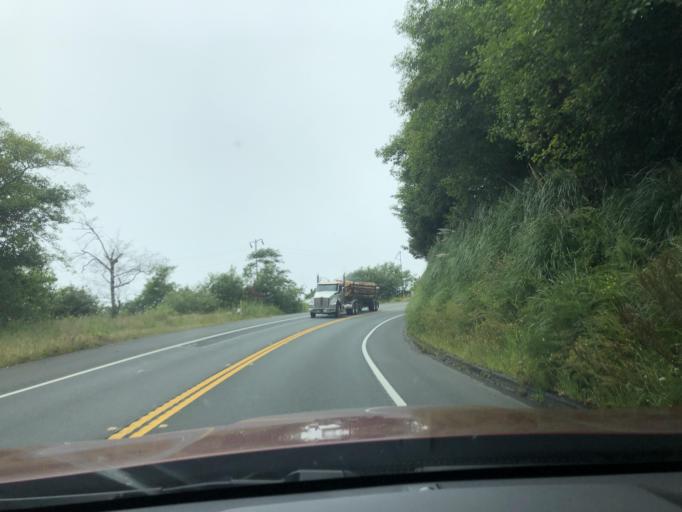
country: US
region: California
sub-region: Humboldt County
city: Westhaven-Moonstone
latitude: 41.2445
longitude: -124.0859
